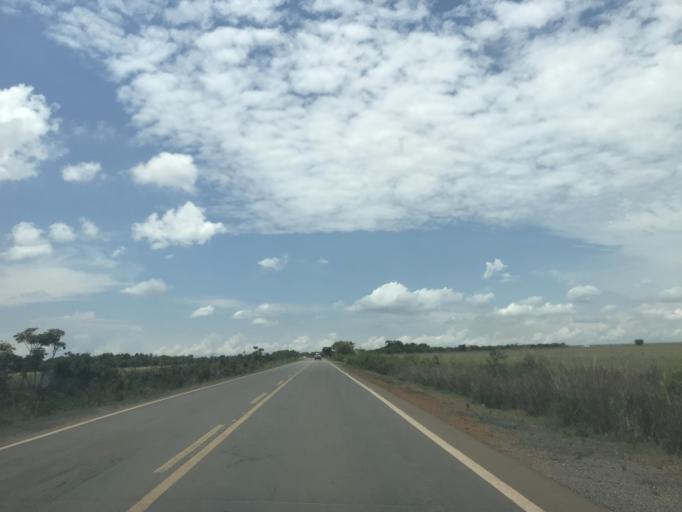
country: BR
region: Goias
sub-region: Vianopolis
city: Vianopolis
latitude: -16.5090
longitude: -48.2286
